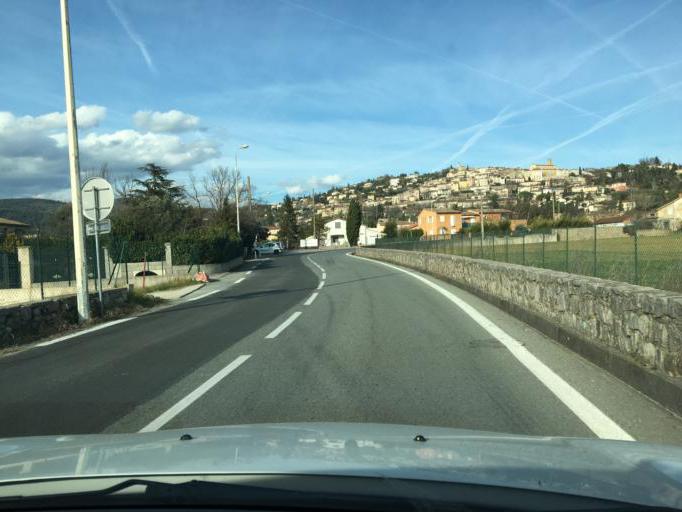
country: FR
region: Provence-Alpes-Cote d'Azur
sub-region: Departement du Var
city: Fayence
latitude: 43.6171
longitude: 6.6881
